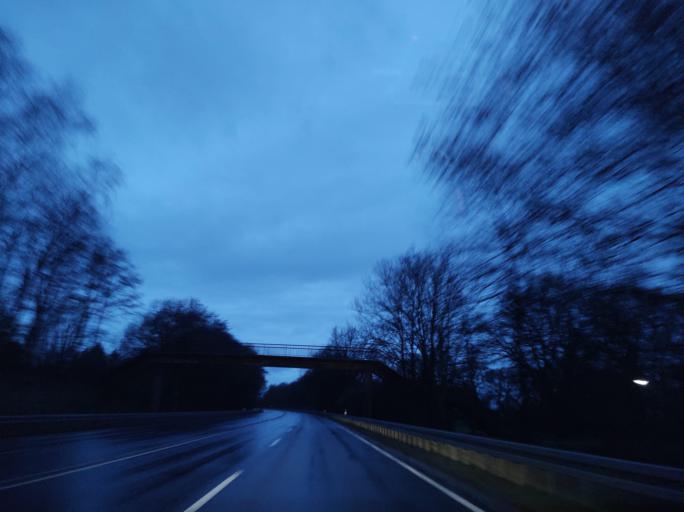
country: DE
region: Lower Saxony
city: Leer
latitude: 53.2396
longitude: 7.4499
